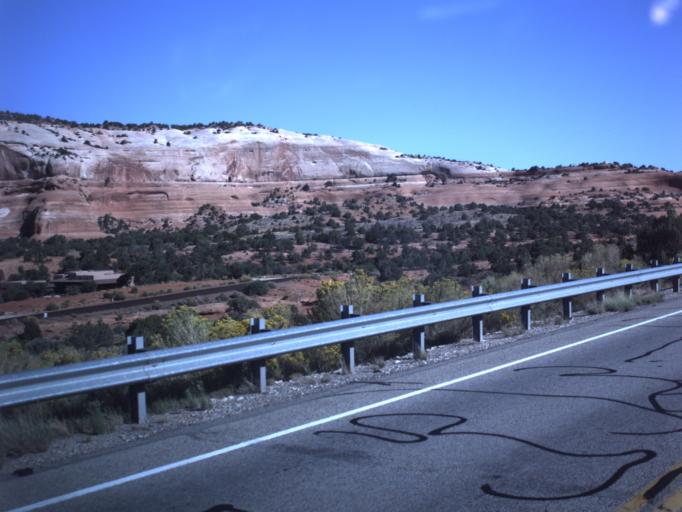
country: US
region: Utah
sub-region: Grand County
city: Moab
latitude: 38.2705
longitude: -109.3741
